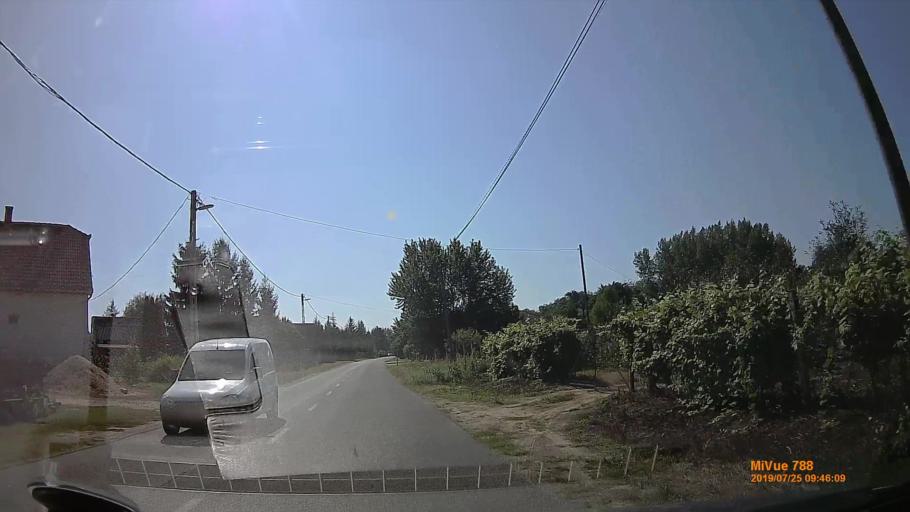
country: HU
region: Szabolcs-Szatmar-Bereg
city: Kotaj
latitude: 48.0330
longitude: 21.7520
